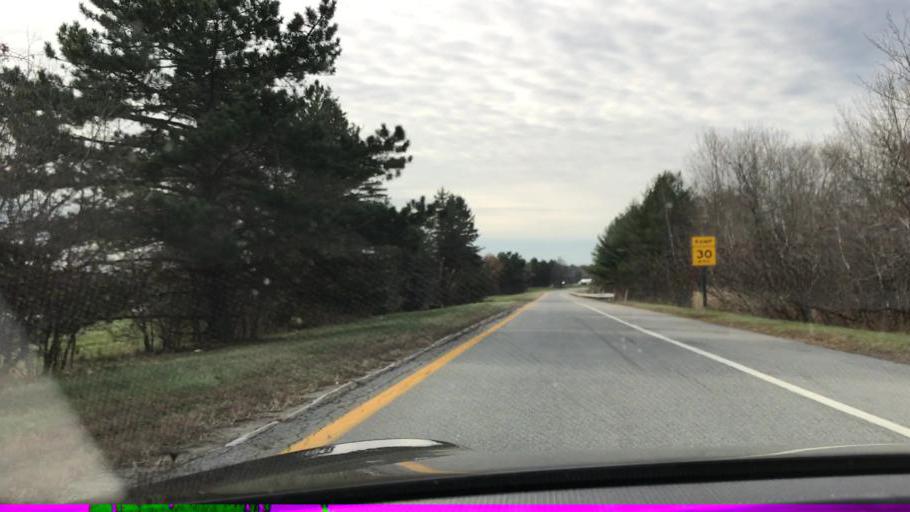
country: US
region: Maine
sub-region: Penobscot County
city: Bangor
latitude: 44.7914
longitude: -68.8056
